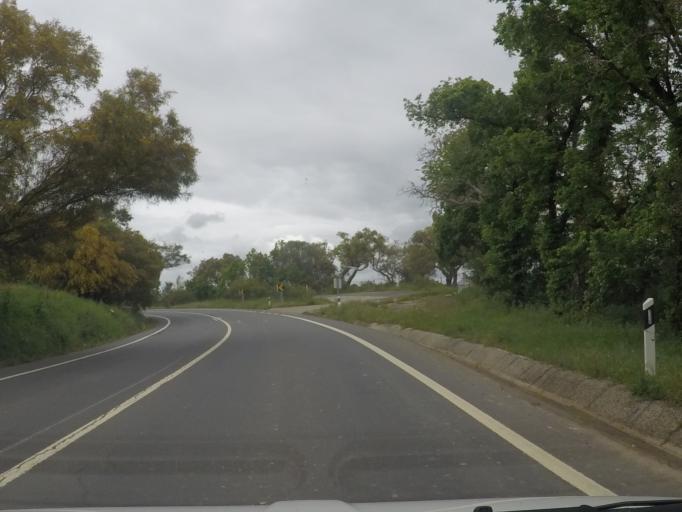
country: PT
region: Setubal
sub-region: Santiago do Cacem
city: Cercal
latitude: 37.8354
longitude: -8.7036
